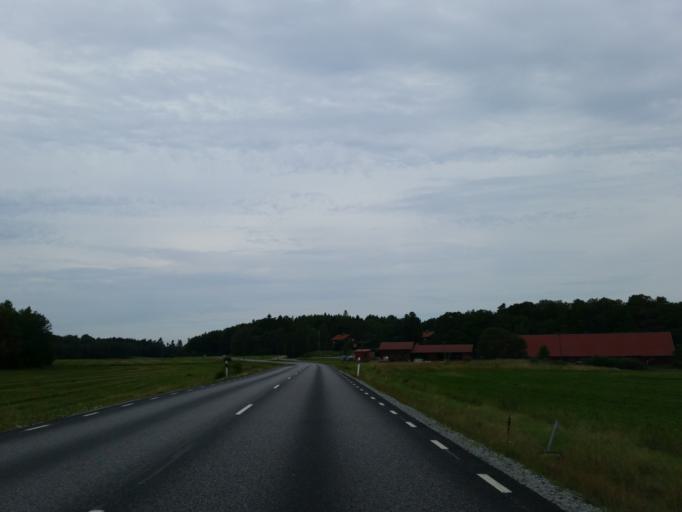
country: SE
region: Stockholm
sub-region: Salems Kommun
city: Ronninge
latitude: 59.2194
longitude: 17.7563
